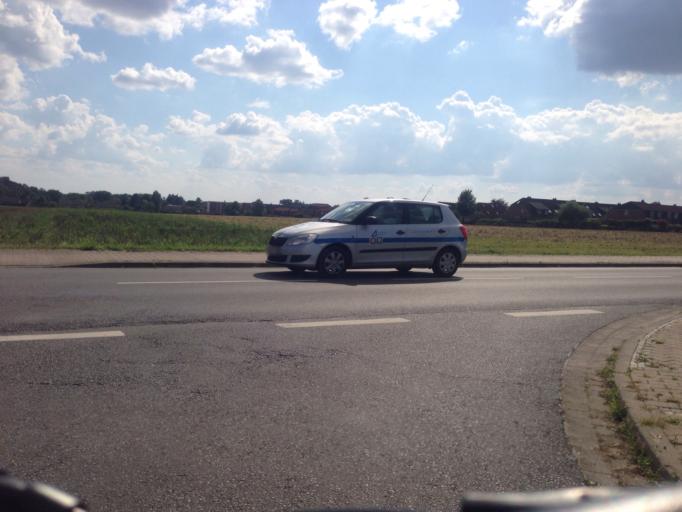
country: DE
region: Lower Saxony
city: Adendorf
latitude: 53.2859
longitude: 10.4469
